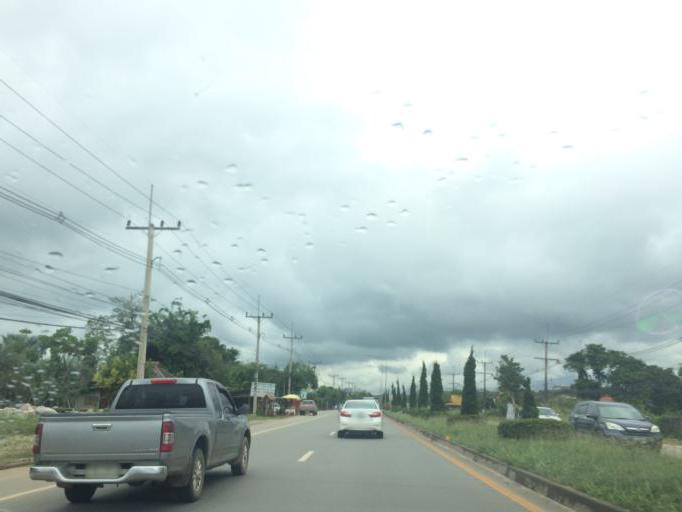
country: TH
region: Chiang Rai
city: Chiang Rai
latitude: 20.0215
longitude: 99.8711
